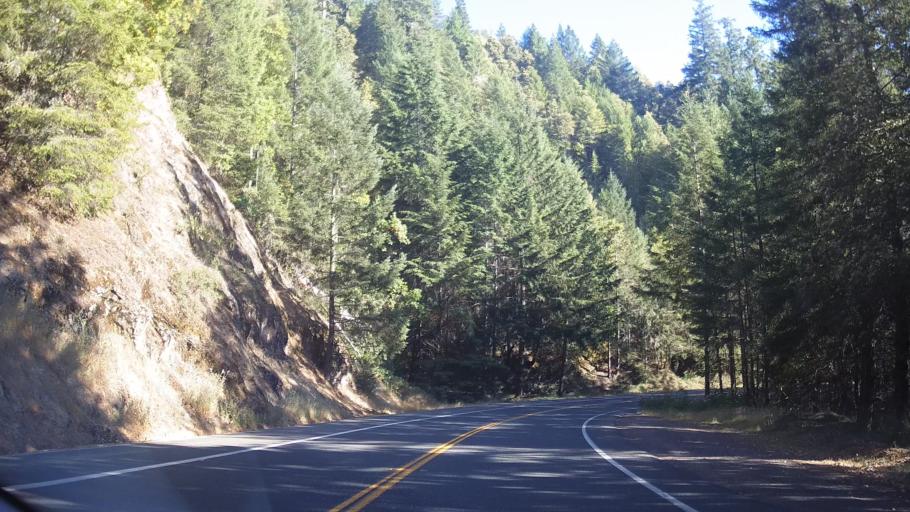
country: US
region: California
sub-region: Mendocino County
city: Brooktrails
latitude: 39.3842
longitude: -123.4739
